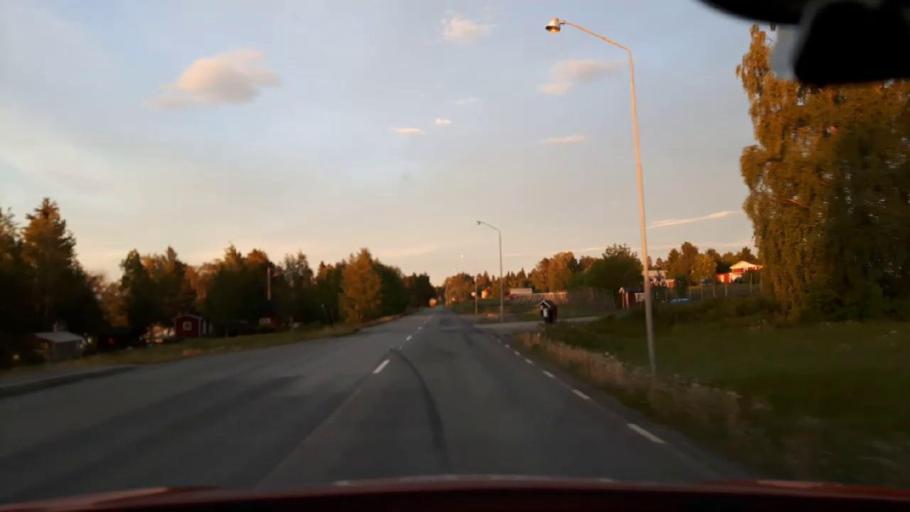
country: SE
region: Jaemtland
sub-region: OEstersunds Kommun
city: Ostersund
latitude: 63.1355
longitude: 14.6415
